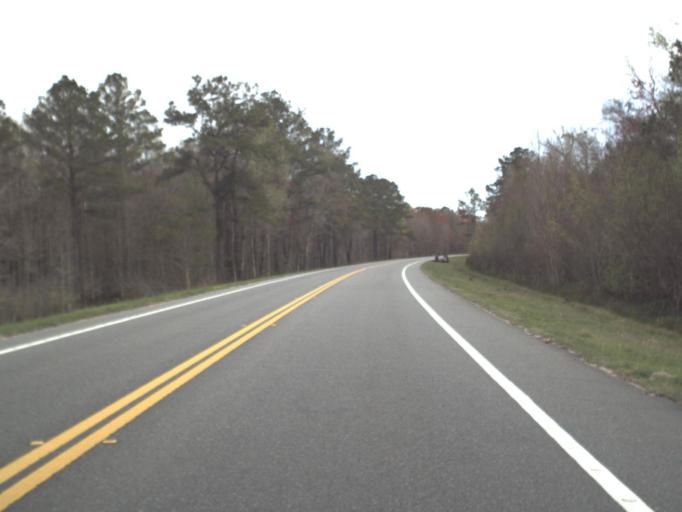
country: US
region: Florida
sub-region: Leon County
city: Woodville
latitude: 30.1805
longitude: -84.0123
